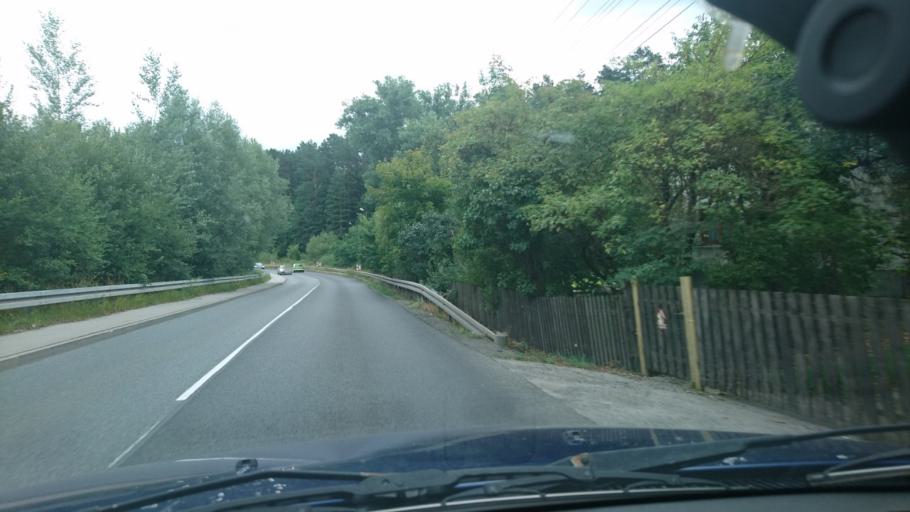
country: PL
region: Silesian Voivodeship
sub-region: Powiat zywiecki
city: Cisiec
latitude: 49.5743
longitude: 19.0998
